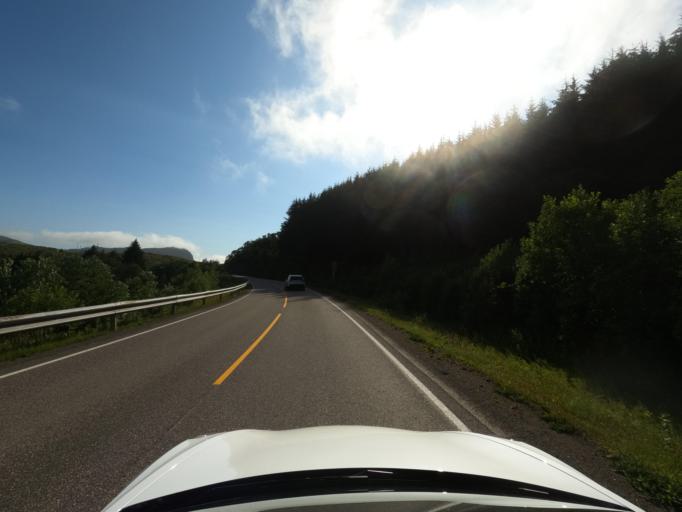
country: NO
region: Nordland
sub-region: Vestvagoy
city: Evjen
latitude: 68.2659
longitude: 13.8324
